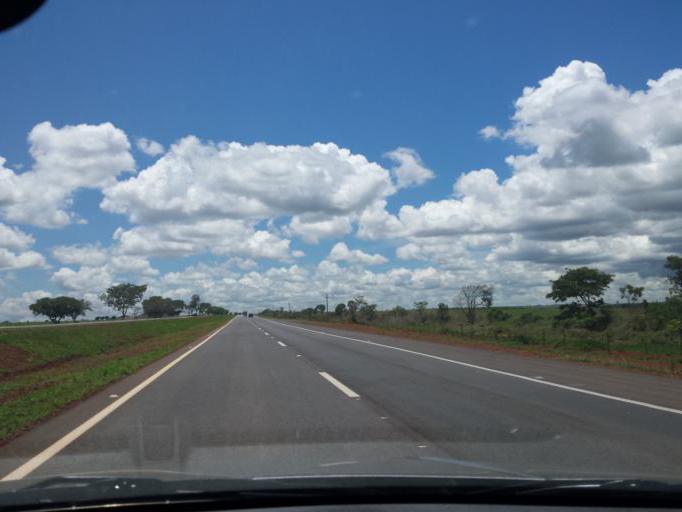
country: BR
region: Goias
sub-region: Cristalina
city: Cristalina
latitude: -16.6928
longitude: -47.6974
